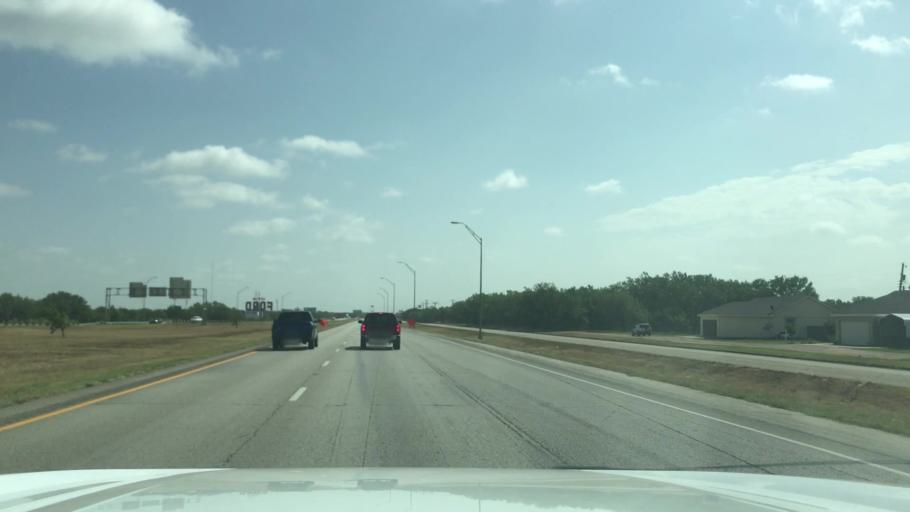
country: US
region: Texas
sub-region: Taylor County
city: Abilene
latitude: 32.4837
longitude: -99.7649
